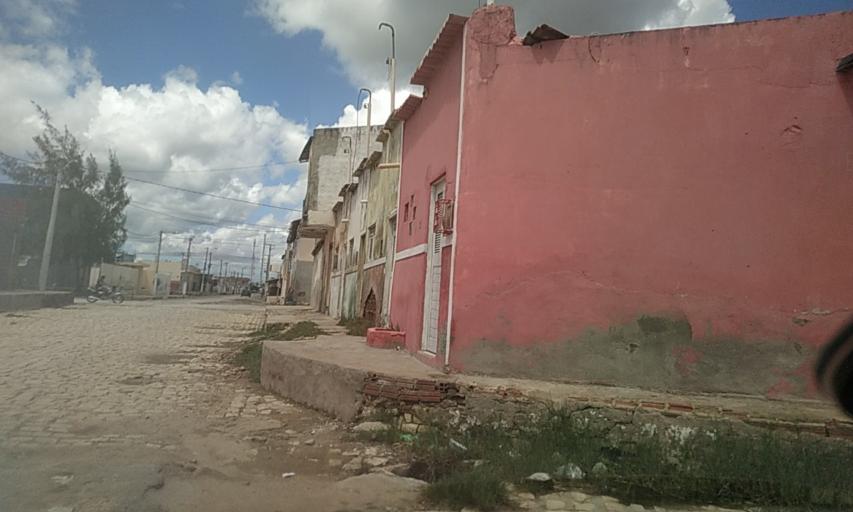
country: BR
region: Rio Grande do Norte
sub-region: Areia Branca
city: Areia Branca
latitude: -4.9507
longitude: -37.1339
